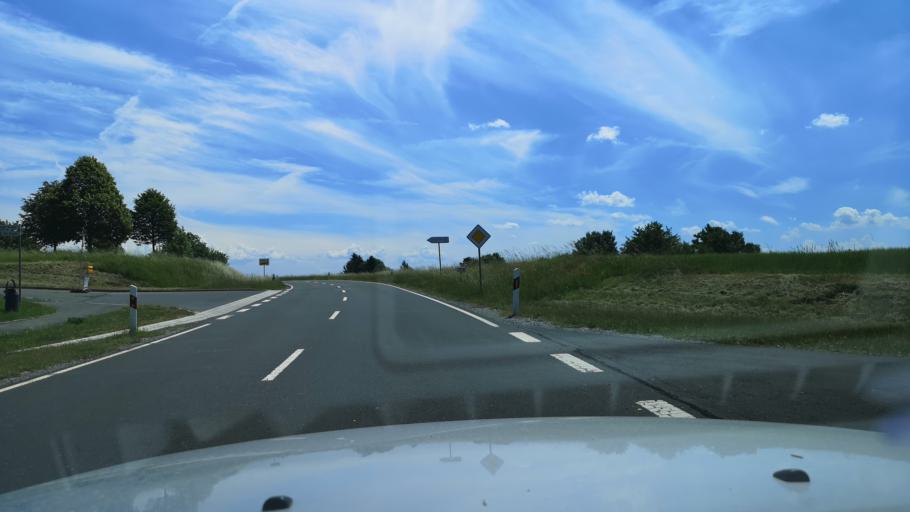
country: DE
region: Bavaria
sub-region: Upper Franconia
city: Teuschnitz
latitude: 50.3958
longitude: 11.3859
